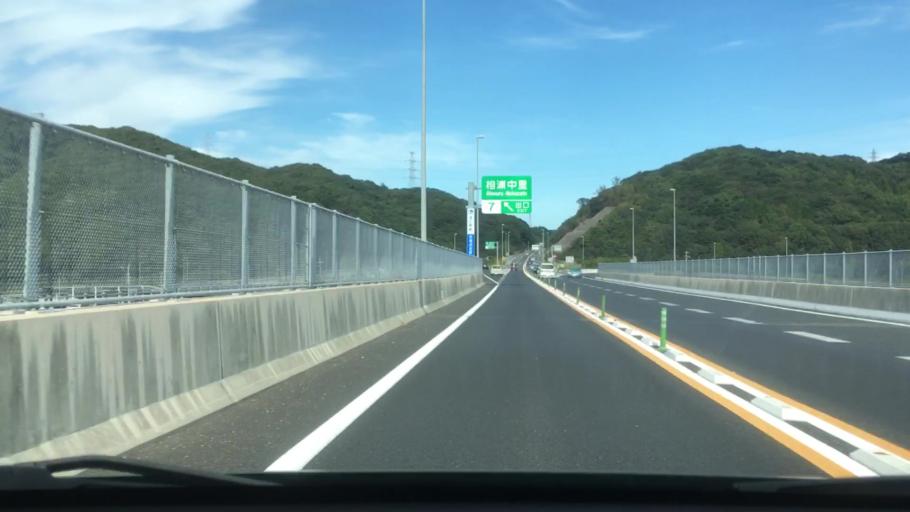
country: JP
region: Nagasaki
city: Sasebo
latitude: 33.2003
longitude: 129.6745
